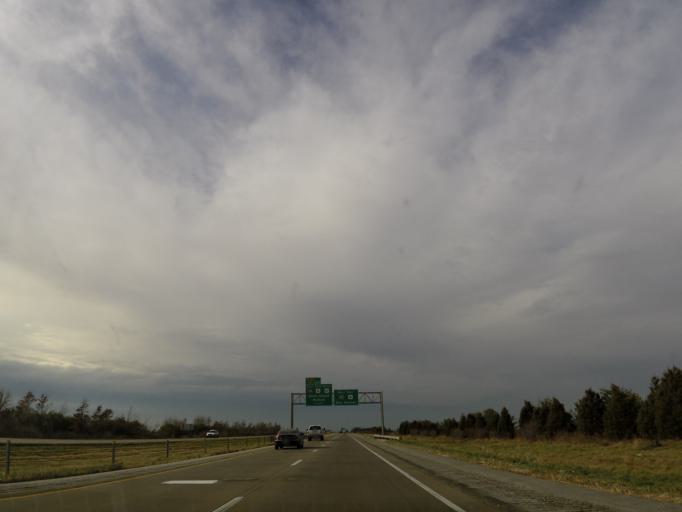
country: US
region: Iowa
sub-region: Scott County
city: Eldridge
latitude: 41.6020
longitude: -90.6486
